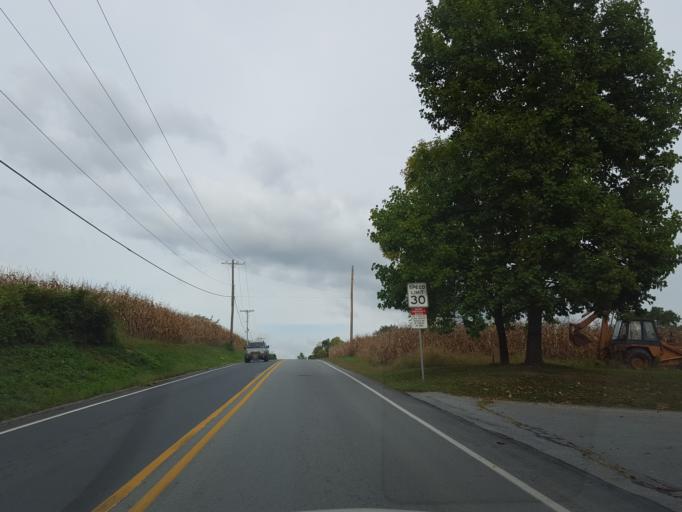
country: US
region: Pennsylvania
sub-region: York County
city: Yoe
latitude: 39.9413
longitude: -76.6547
